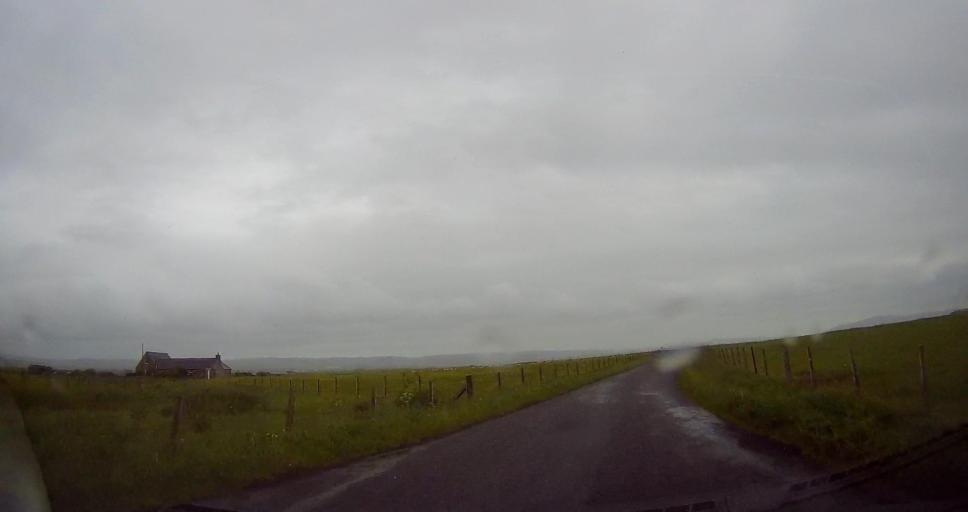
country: GB
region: Scotland
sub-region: Orkney Islands
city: Stromness
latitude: 59.0697
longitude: -3.2840
